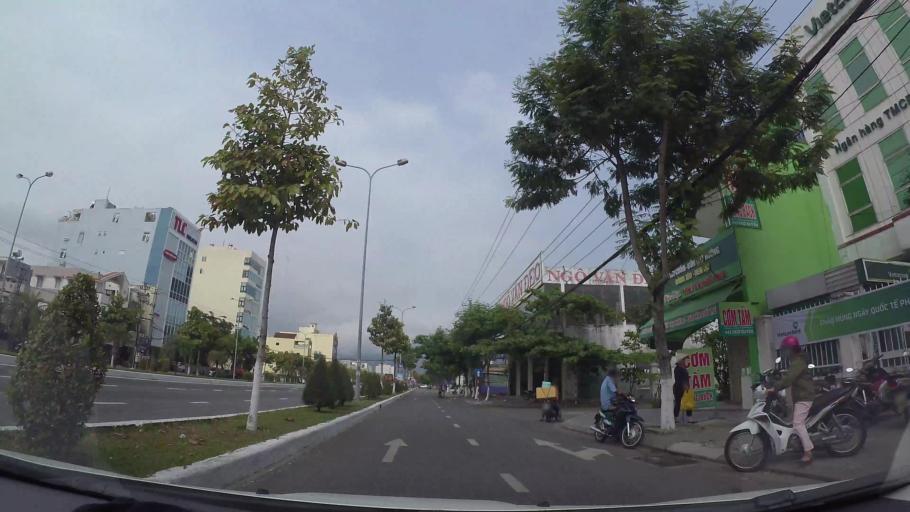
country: VN
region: Da Nang
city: Da Nang
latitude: 16.0811
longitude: 108.2354
